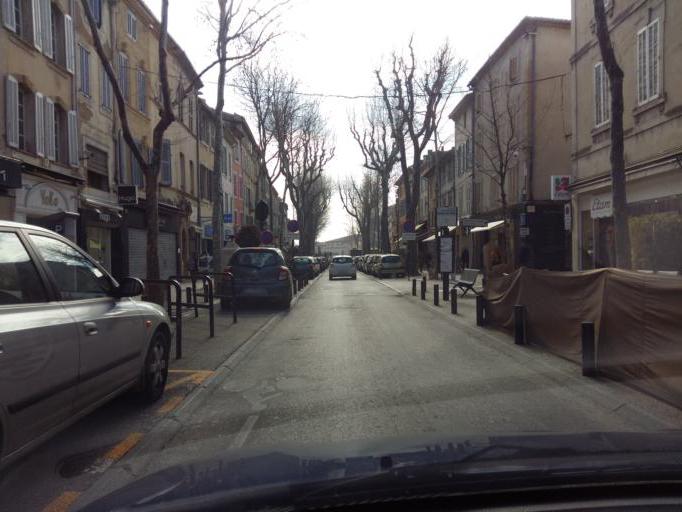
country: FR
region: Provence-Alpes-Cote d'Azur
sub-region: Departement des Bouches-du-Rhone
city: Salon-de-Provence
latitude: 43.6403
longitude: 5.0990
